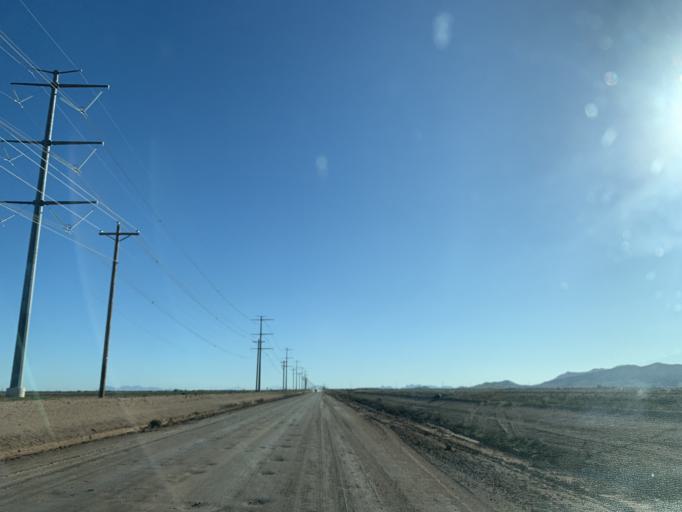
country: US
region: Arizona
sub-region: Pinal County
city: Casa Grande
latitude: 32.8631
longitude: -111.6709
